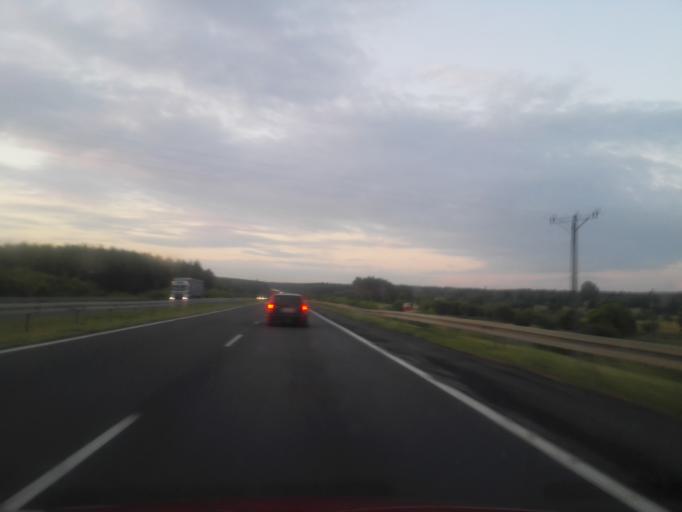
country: PL
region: Lodz Voivodeship
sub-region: Powiat radomszczanski
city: Gomunice
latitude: 51.1503
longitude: 19.4381
